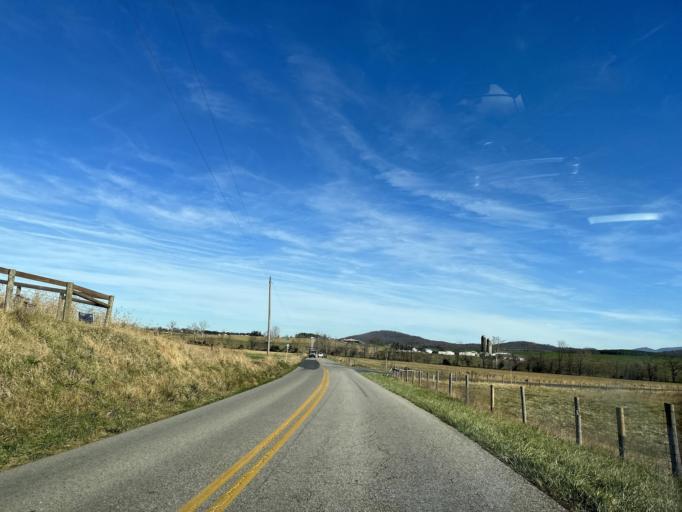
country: US
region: Virginia
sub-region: Augusta County
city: Crimora
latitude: 38.1617
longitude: -78.9218
